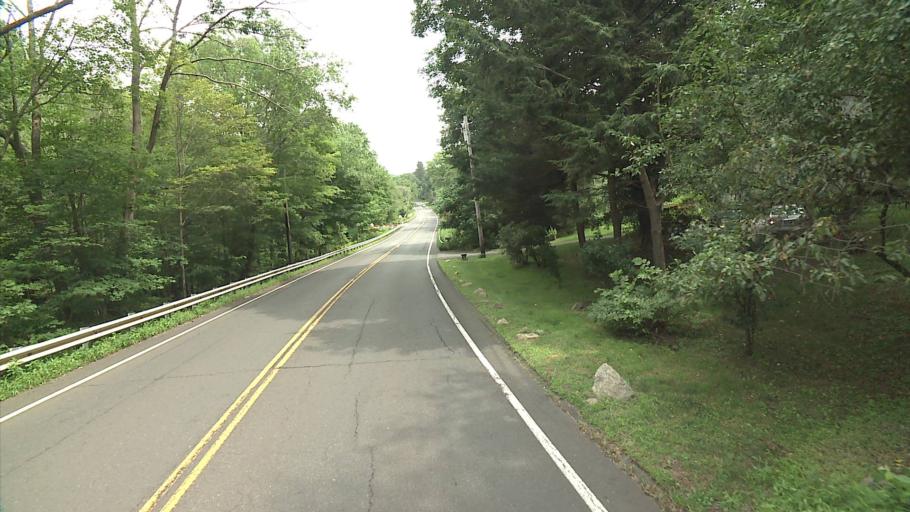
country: US
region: Connecticut
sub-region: New Haven County
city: Seymour
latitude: 41.3918
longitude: -73.0385
